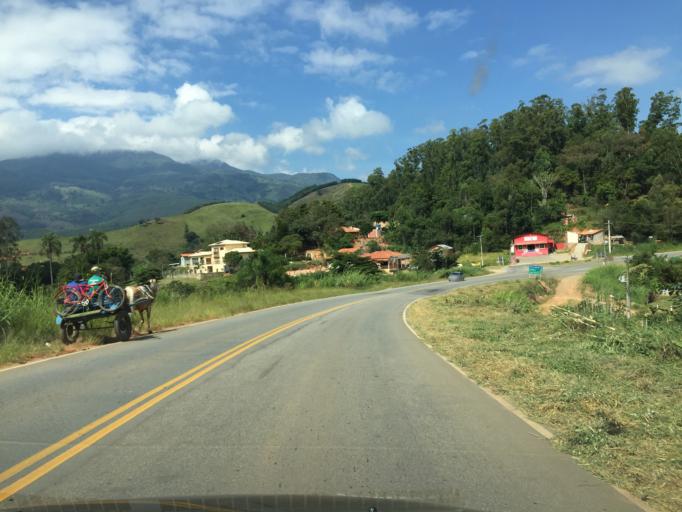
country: BR
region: Minas Gerais
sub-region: Passa Quatro
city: Passa Quatro
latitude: -22.3732
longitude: -44.9618
